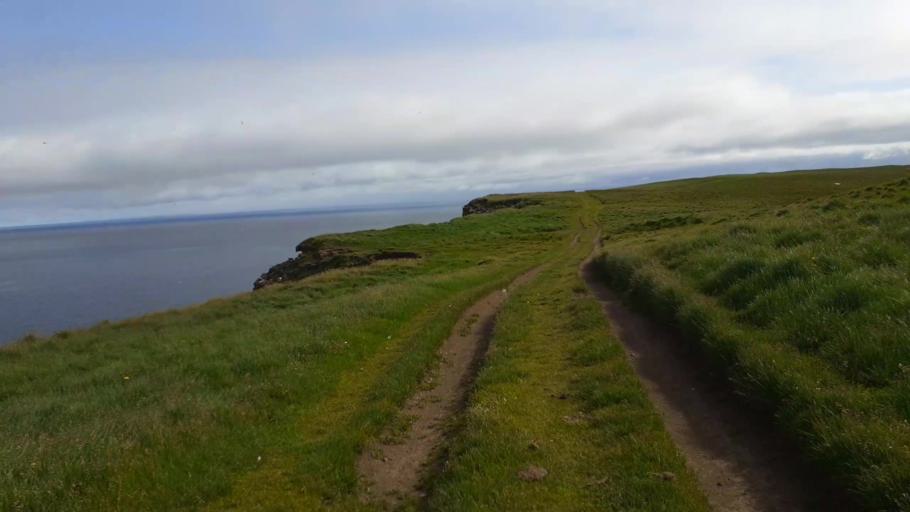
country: IS
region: Northeast
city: Dalvik
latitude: 66.5528
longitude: -17.9977
